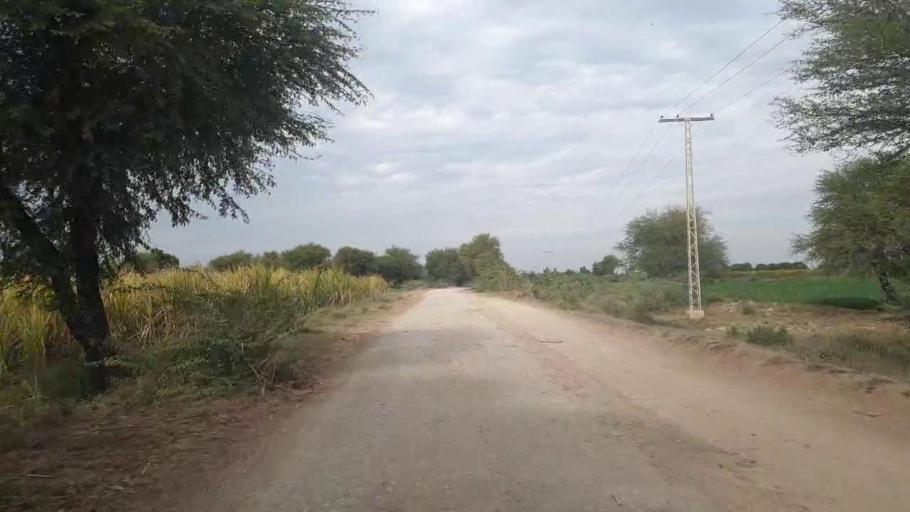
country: PK
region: Sindh
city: Sinjhoro
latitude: 26.0210
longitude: 68.8748
